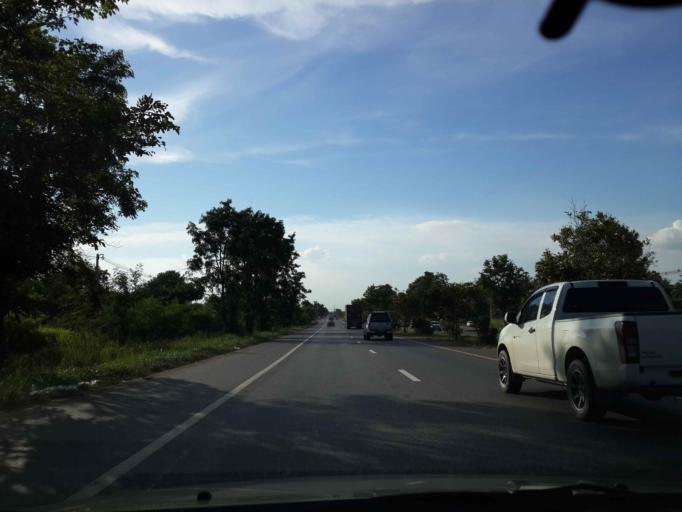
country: TH
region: Chon Buri
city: Phatthaya
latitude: 12.9362
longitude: 100.9978
